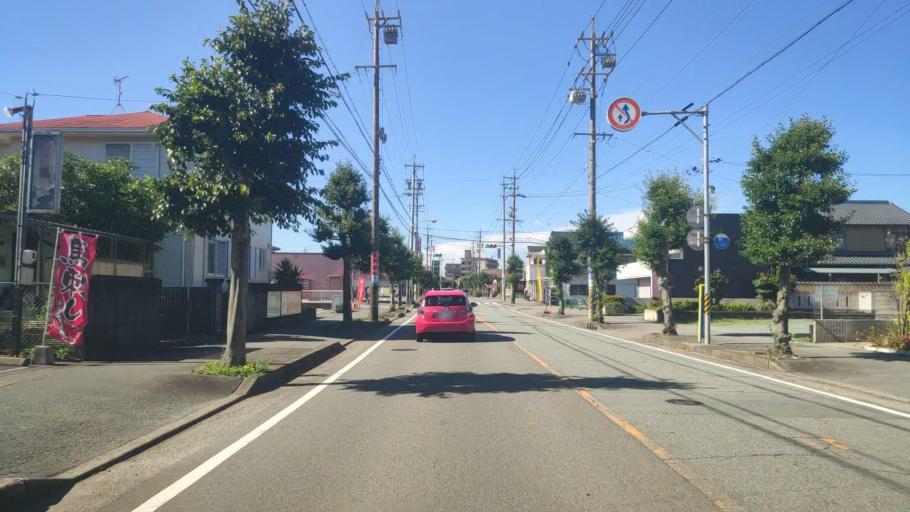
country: JP
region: Mie
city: Ise
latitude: 34.5007
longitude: 136.7073
